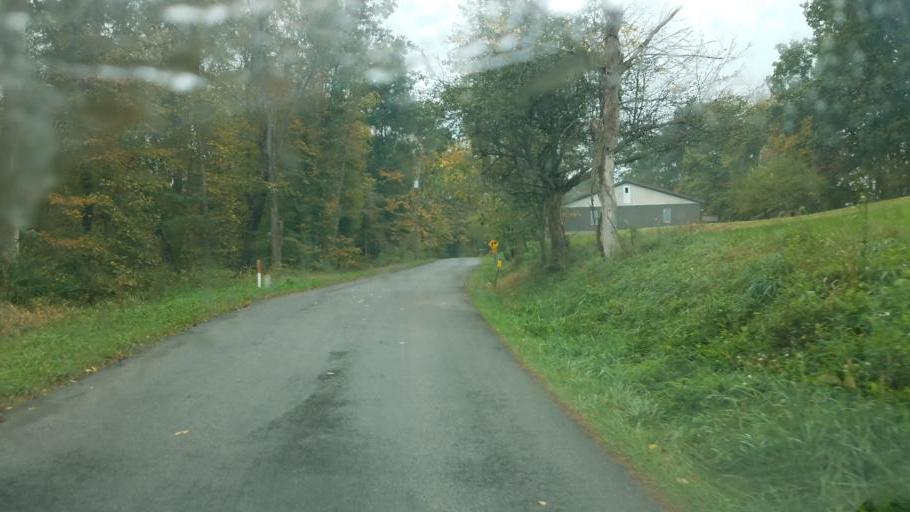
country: US
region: Ohio
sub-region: Holmes County
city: Millersburg
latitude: 40.5619
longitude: -81.8875
